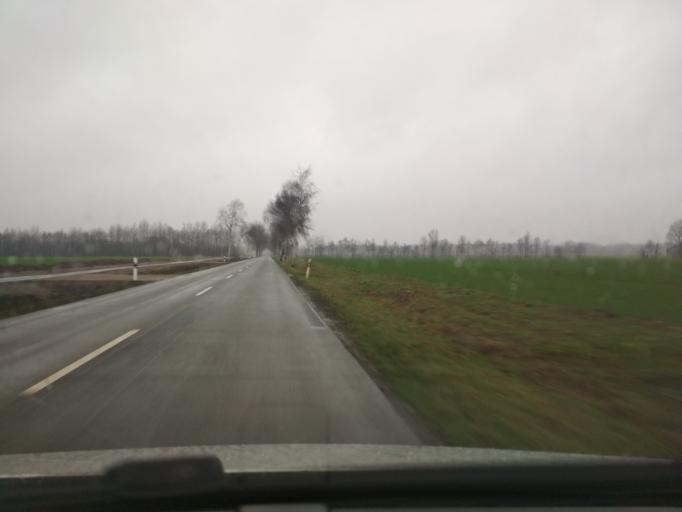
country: DE
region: Lower Saxony
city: Wittingen
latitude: 52.6932
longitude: 10.6774
